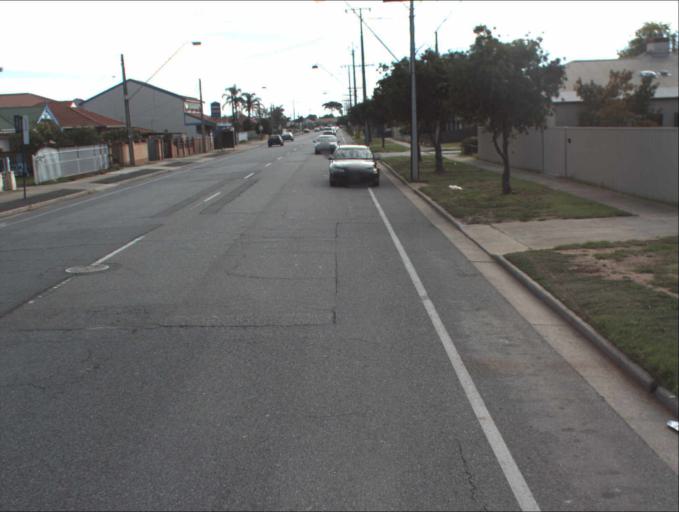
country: AU
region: South Australia
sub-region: Port Adelaide Enfield
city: Alberton
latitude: -34.8556
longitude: 138.5291
